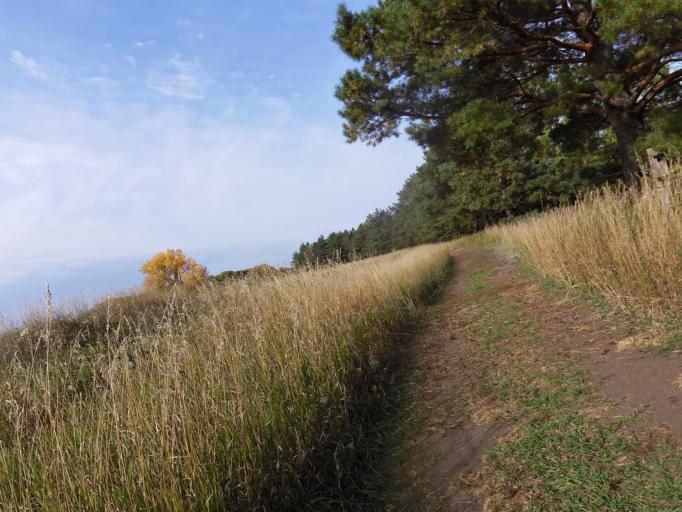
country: US
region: North Dakota
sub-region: Pembina County
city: Cavalier
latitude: 48.7809
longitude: -97.7462
